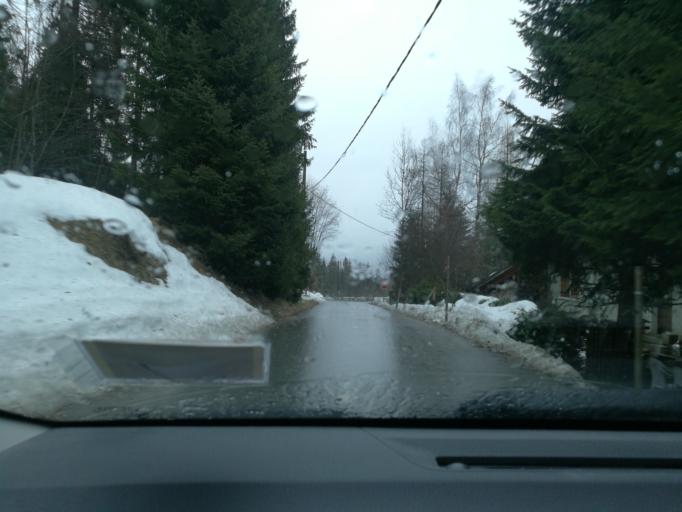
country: FR
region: Rhone-Alpes
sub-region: Departement de la Haute-Savoie
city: Saint-Gervais-les-Bains
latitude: 45.8708
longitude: 6.6922
